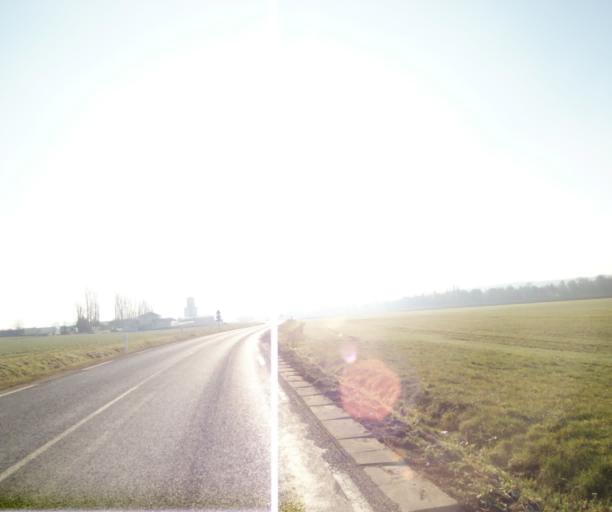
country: FR
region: Champagne-Ardenne
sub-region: Departement de la Haute-Marne
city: Wassy
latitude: 48.5163
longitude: 4.9359
